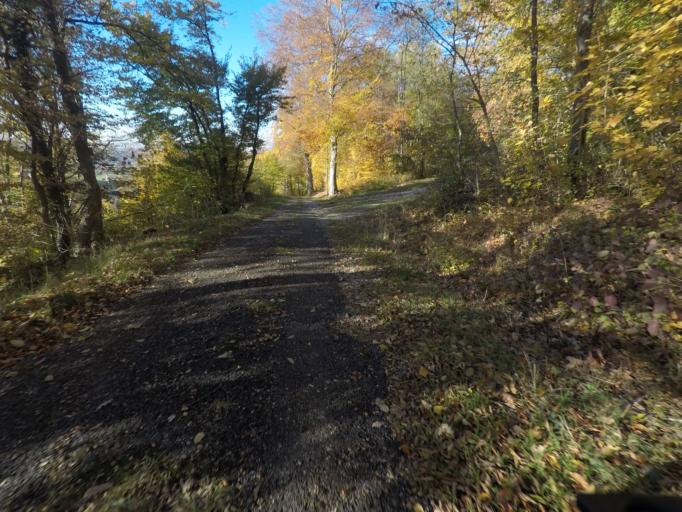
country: DE
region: Baden-Wuerttemberg
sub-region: Tuebingen Region
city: Pfullingen
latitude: 48.4407
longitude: 9.2164
